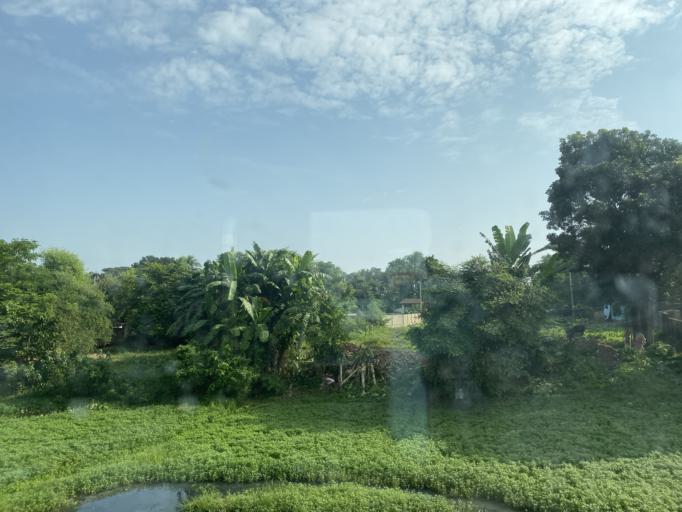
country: BD
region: Dhaka
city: Bhairab Bazar
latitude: 23.9630
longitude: 91.1178
